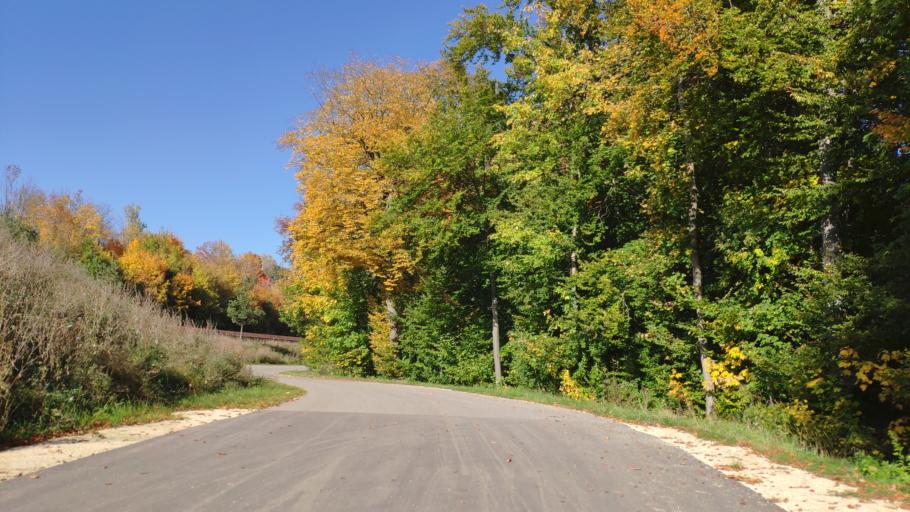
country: DE
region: Baden-Wuerttemberg
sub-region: Tuebingen Region
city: Ulm
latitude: 48.4126
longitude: 9.9845
